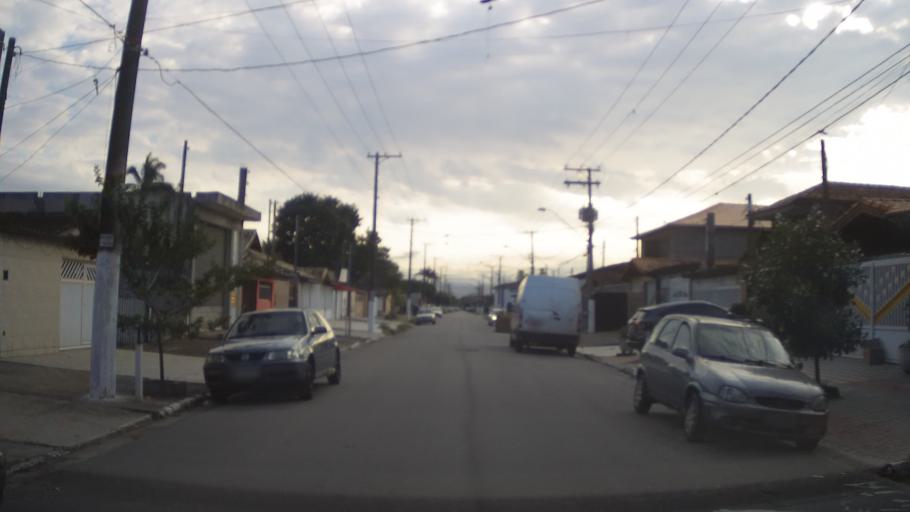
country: BR
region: Sao Paulo
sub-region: Praia Grande
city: Praia Grande
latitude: -23.9992
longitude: -46.4195
